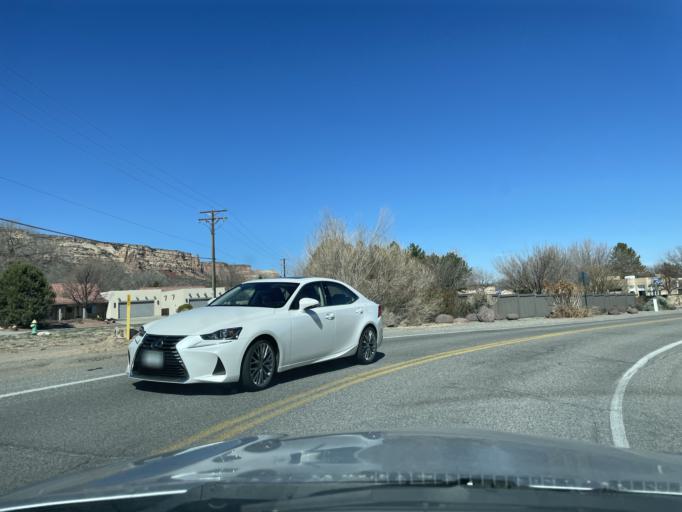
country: US
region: Colorado
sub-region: Mesa County
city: Redlands
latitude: 39.0743
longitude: -108.6640
